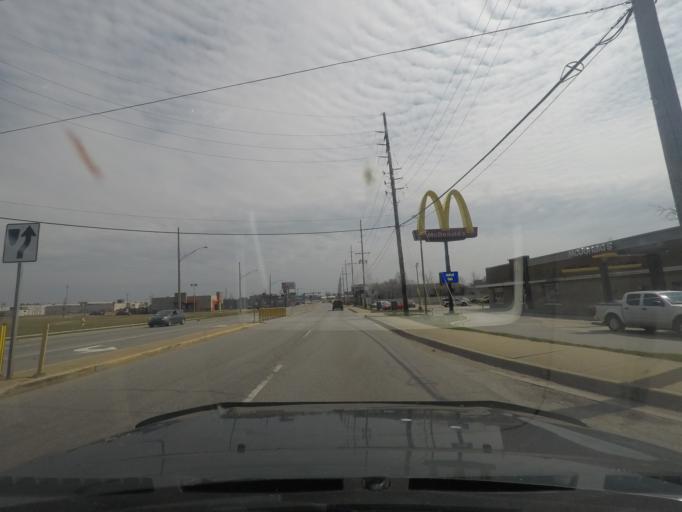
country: US
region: Indiana
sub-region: LaPorte County
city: LaPorte
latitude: 41.6160
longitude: -86.7320
